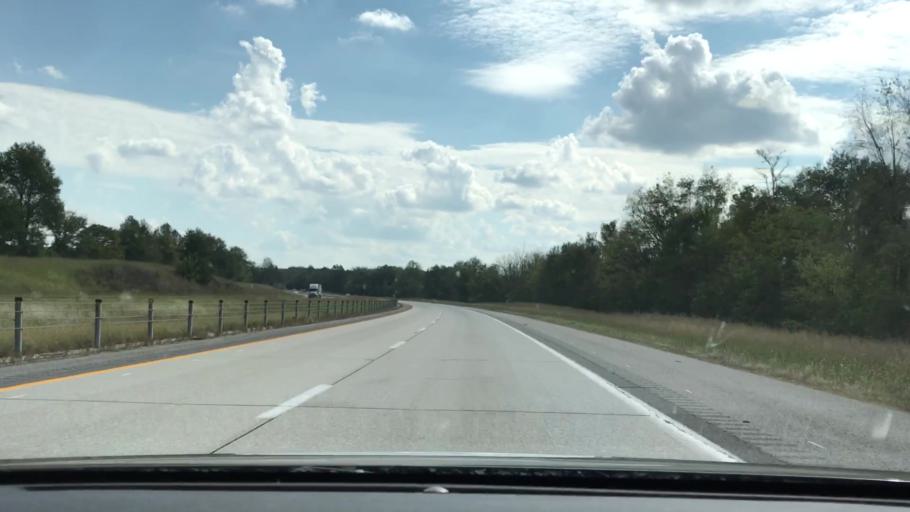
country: US
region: Kentucky
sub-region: Trigg County
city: Cadiz
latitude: 36.8558
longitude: -87.7030
